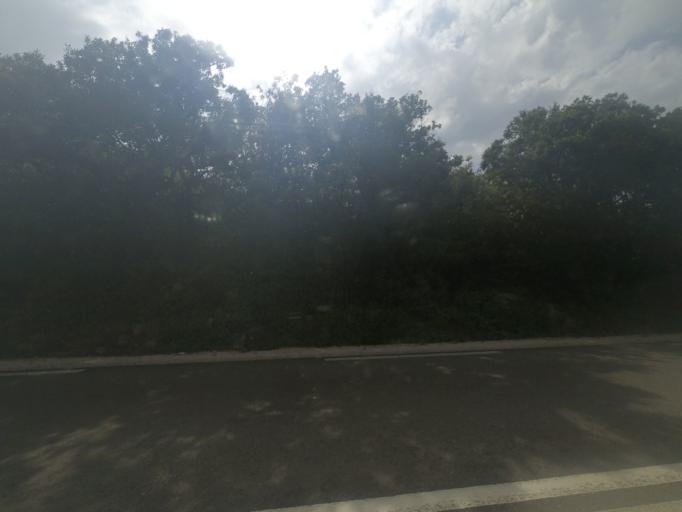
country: FR
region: Languedoc-Roussillon
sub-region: Departement de l'Herault
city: Les Matelles
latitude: 43.7361
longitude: 3.7890
